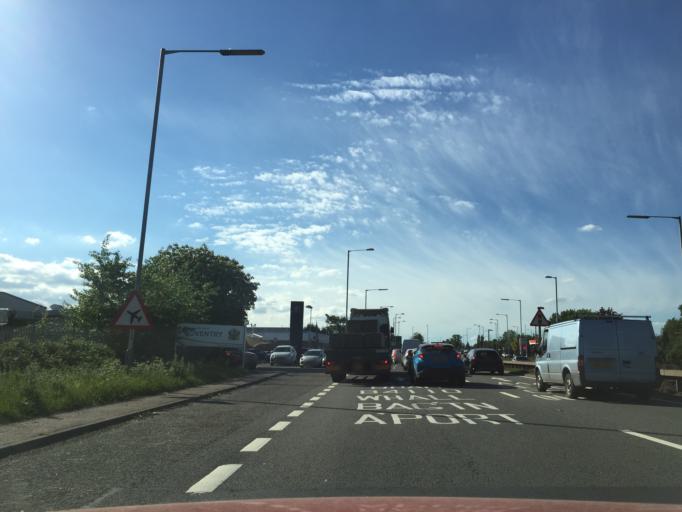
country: GB
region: England
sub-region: Warwickshire
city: Ryton on Dunsmore
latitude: 52.3761
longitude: -1.4626
